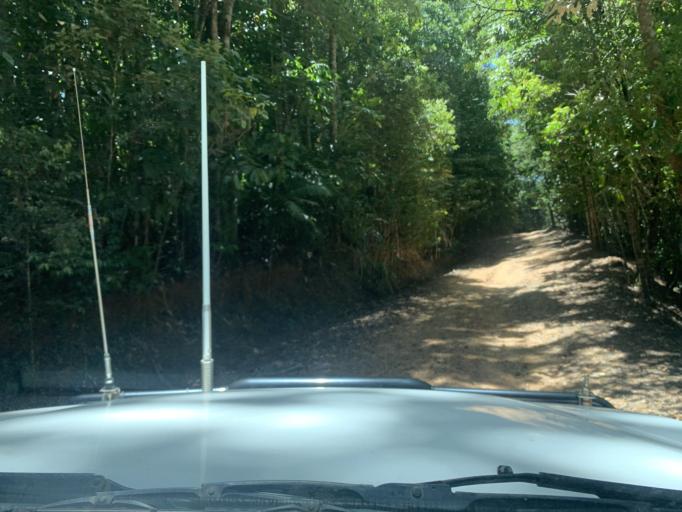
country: AU
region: Queensland
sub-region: Cairns
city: Redlynch
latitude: -16.9550
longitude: 145.6383
